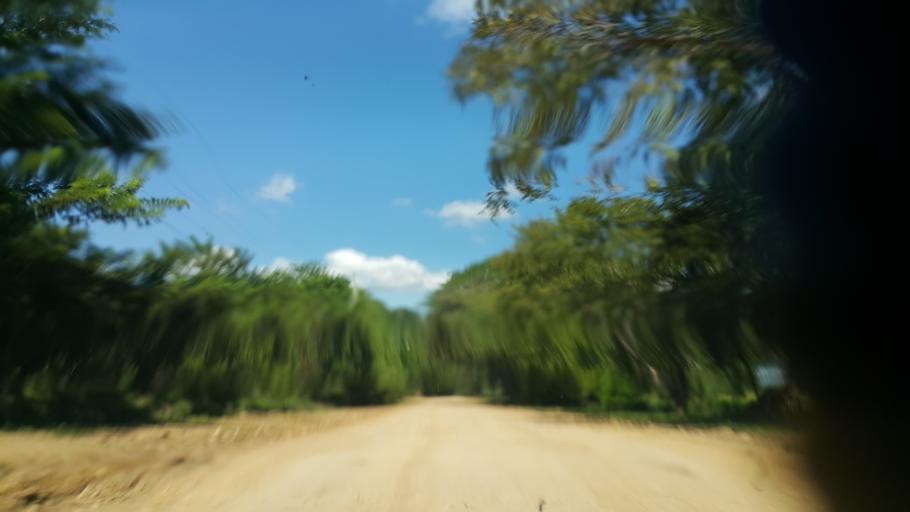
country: NI
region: Rivas
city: San Juan del Sur
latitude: 11.2873
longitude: -85.8900
